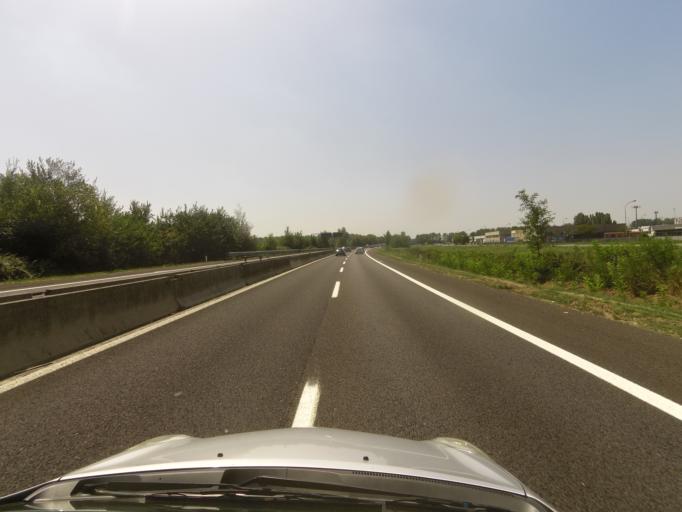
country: IT
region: Emilia-Romagna
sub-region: Provincia di Ferrara
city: Porotto-Cassama
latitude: 44.8601
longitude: 11.5699
